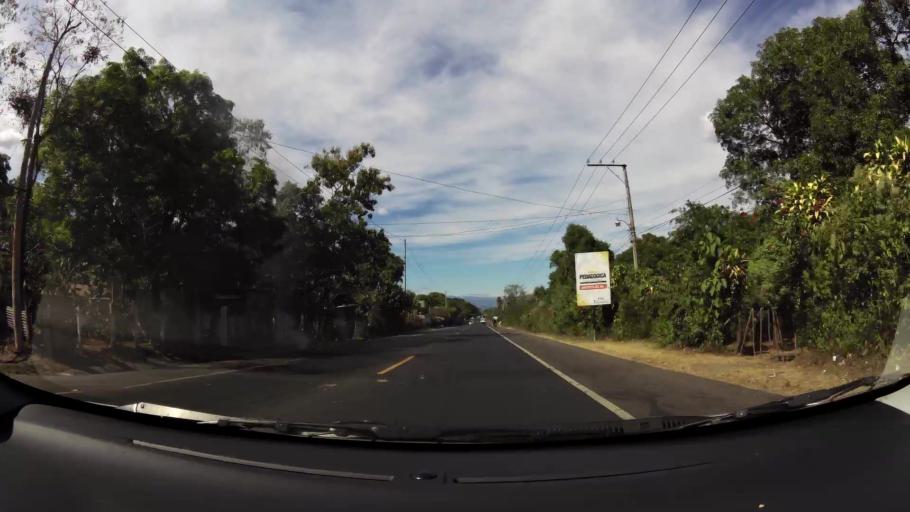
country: SV
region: San Salvador
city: Guazapa
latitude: 13.8829
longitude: -89.1749
